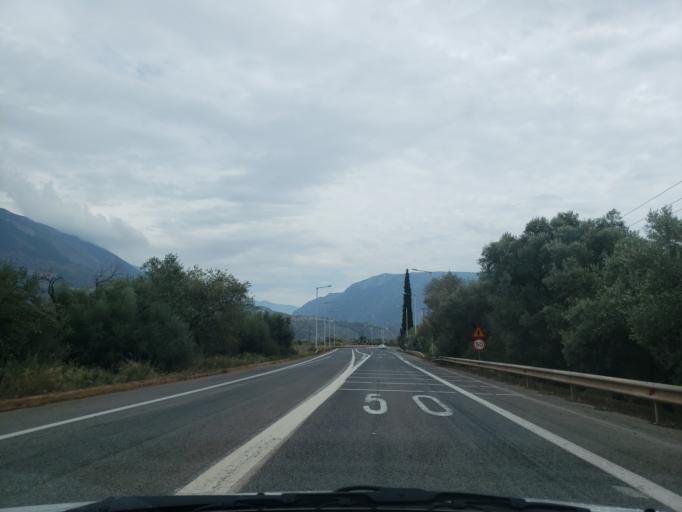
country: GR
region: Central Greece
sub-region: Nomos Fokidos
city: Itea
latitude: 38.4815
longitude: 22.4317
